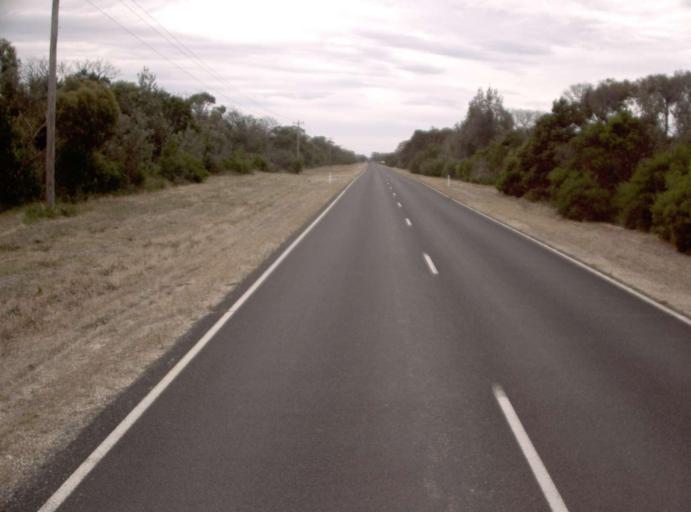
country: AU
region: Victoria
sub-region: East Gippsland
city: Bairnsdale
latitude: -38.0658
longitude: 147.5561
